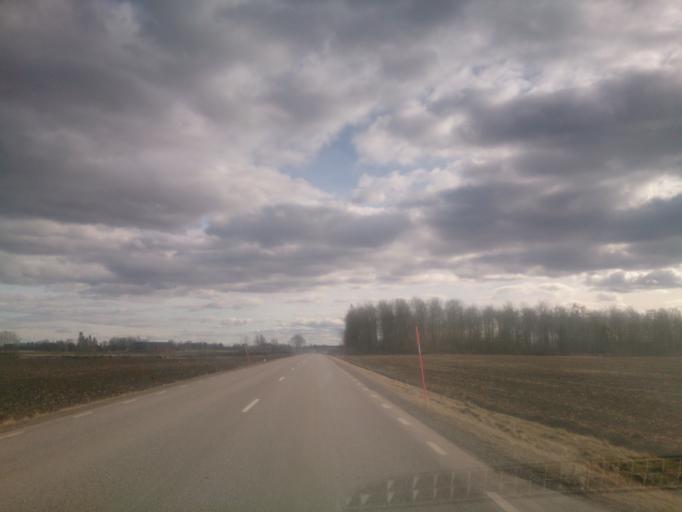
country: SE
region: OEstergoetland
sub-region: Motala Kommun
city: Borensberg
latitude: 58.4987
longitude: 15.2049
